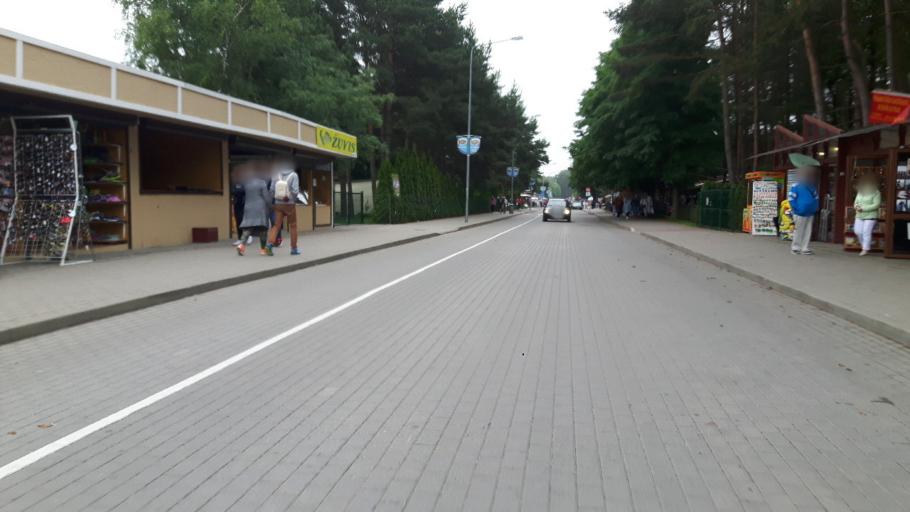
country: LT
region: Klaipedos apskritis
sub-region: Palanga
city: Sventoji
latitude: 56.0334
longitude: 21.0779
